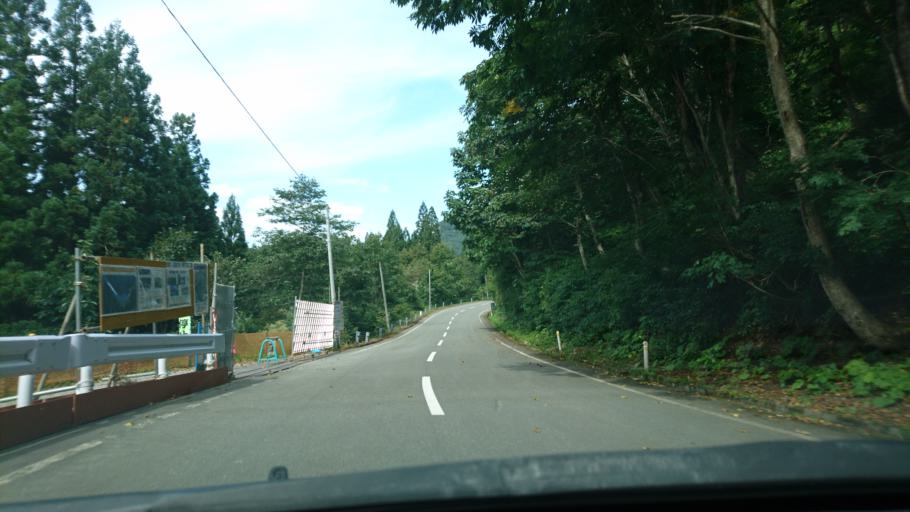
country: JP
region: Akita
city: Yuzawa
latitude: 39.0267
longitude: 140.7280
